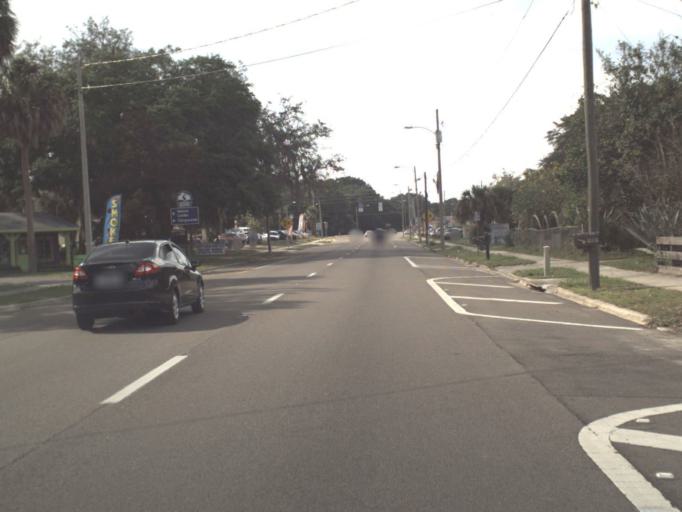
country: US
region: Florida
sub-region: Lake County
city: Eustis
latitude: 28.8622
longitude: -81.6845
